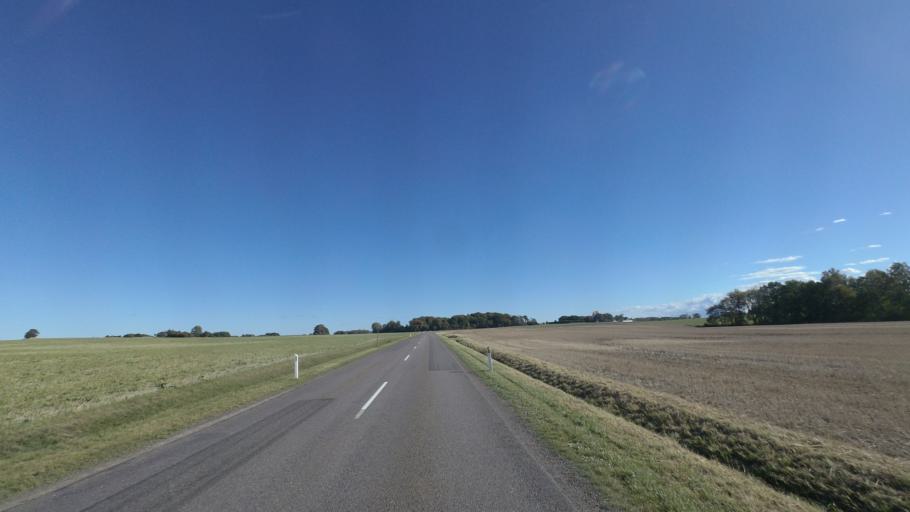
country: DK
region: Capital Region
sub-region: Bornholm Kommune
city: Nexo
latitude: 55.1223
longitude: 15.0964
